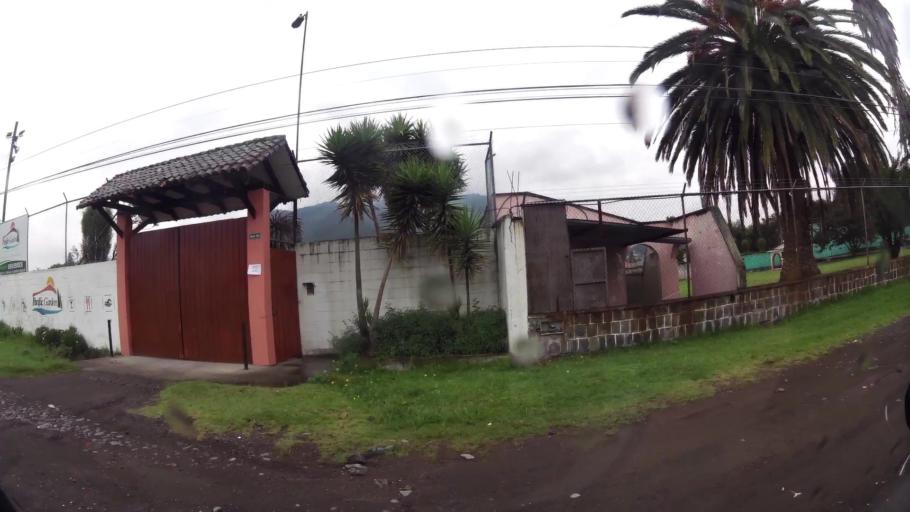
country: EC
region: Pichincha
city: Sangolqui
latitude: -0.2864
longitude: -78.4505
